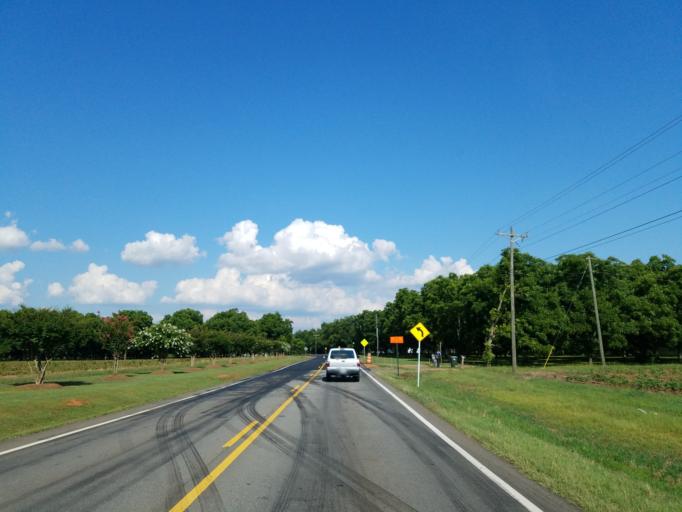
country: US
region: Georgia
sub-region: Peach County
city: Fort Valley
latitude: 32.5544
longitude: -83.8260
